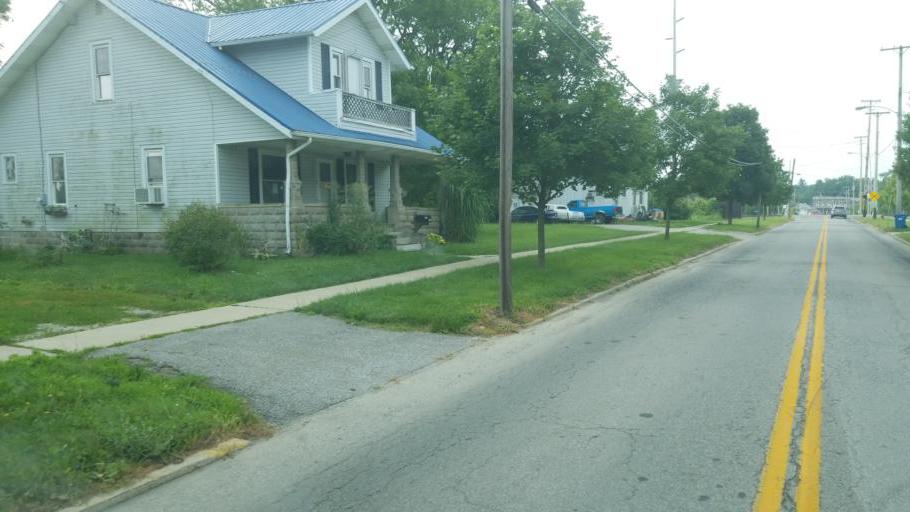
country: US
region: Ohio
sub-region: Morrow County
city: Cardington
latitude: 40.5035
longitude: -82.8955
